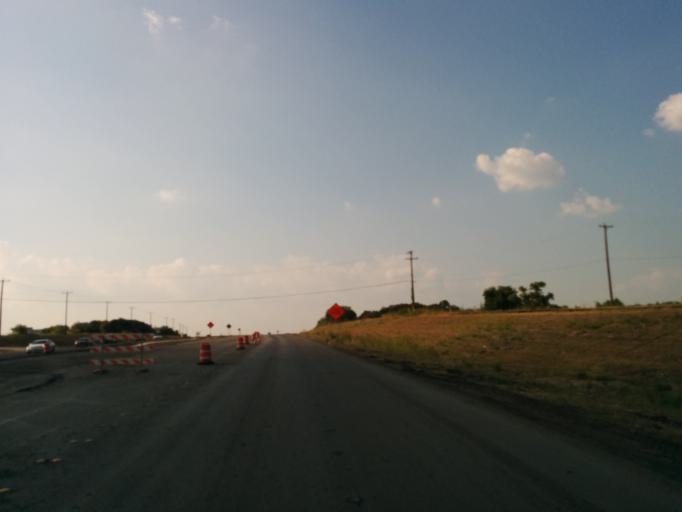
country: US
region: Texas
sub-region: Bexar County
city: Converse
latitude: 29.4667
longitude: -98.2925
